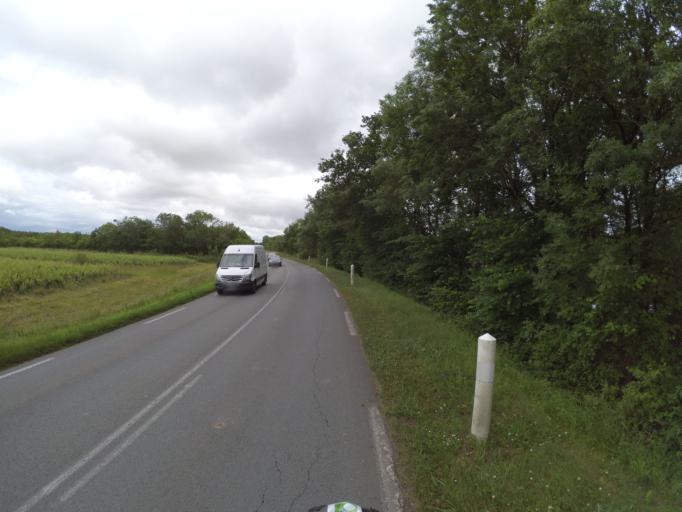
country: FR
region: Aquitaine
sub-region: Departement de la Gironde
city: Cantenac
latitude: 45.0260
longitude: -0.6458
